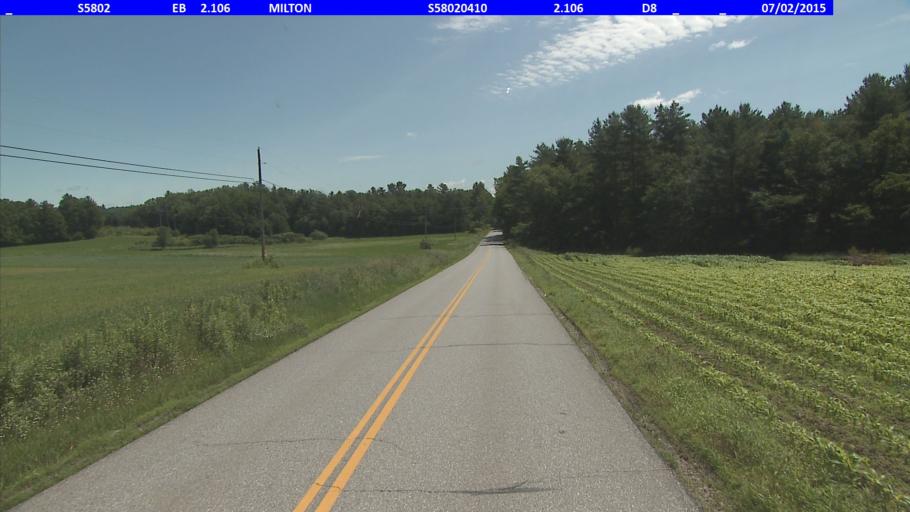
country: US
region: Vermont
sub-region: Chittenden County
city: Milton
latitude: 44.6314
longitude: -73.1852
